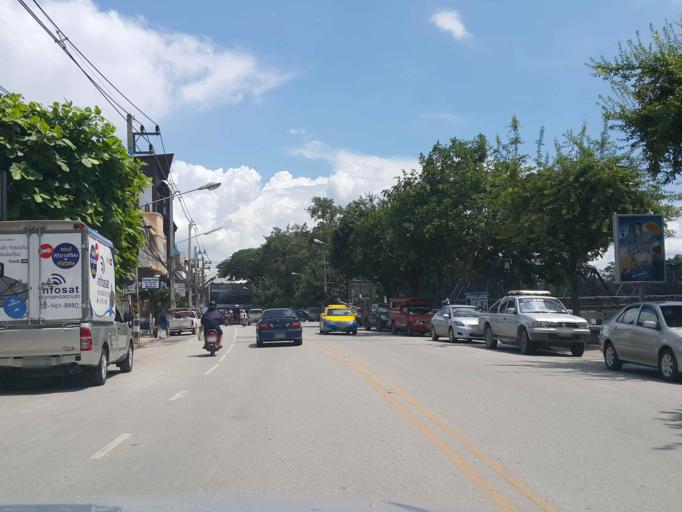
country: TH
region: Chiang Mai
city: Chiang Mai
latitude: 18.7848
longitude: 99.0050
